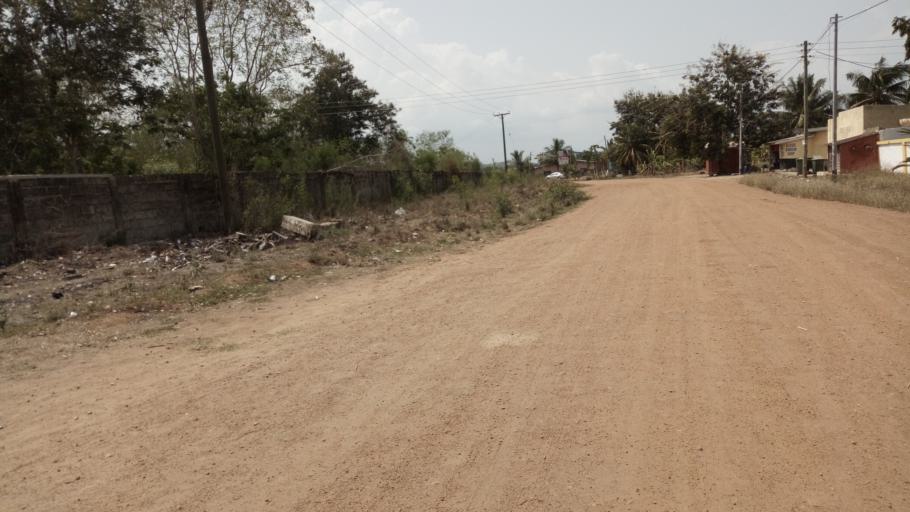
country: GH
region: Central
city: Winneba
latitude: 5.3573
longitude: -0.6365
